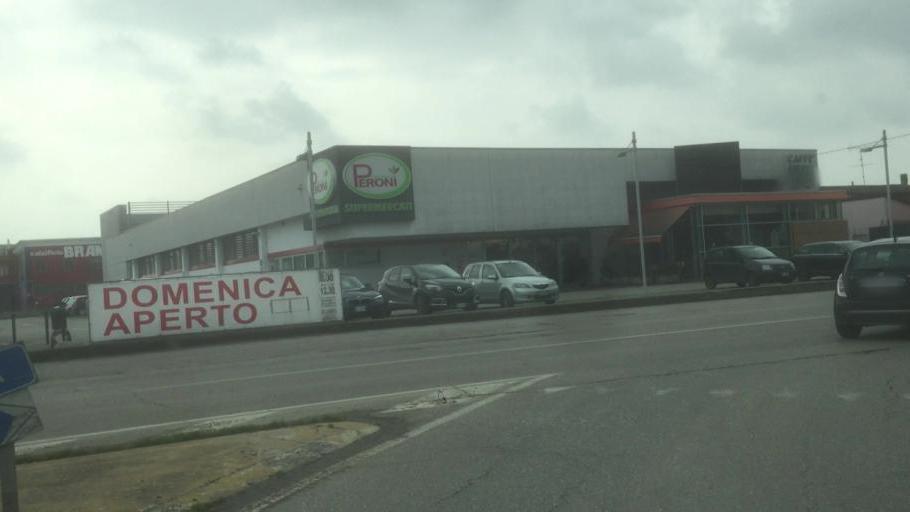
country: IT
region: Lombardy
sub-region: Provincia di Mantova
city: Casaloldo
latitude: 45.2545
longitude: 10.4732
